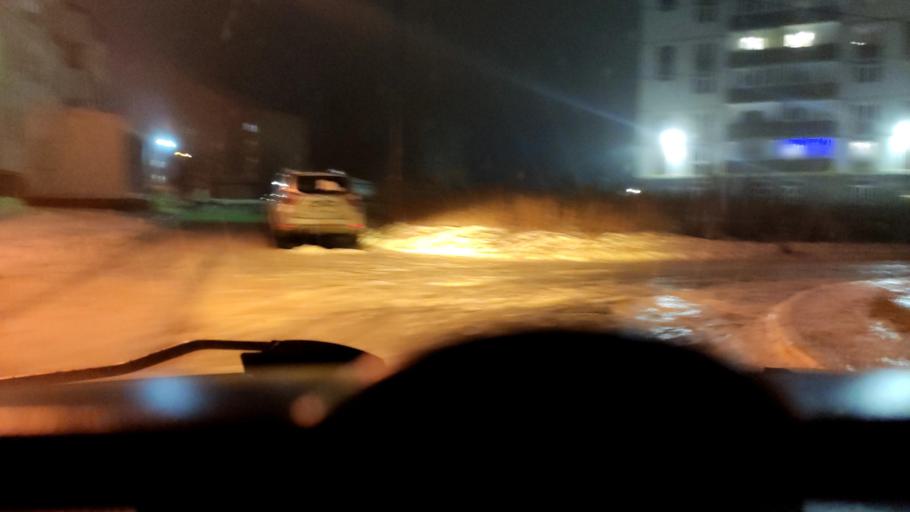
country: RU
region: Voronezj
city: Semiluki
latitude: 51.6933
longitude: 39.0051
